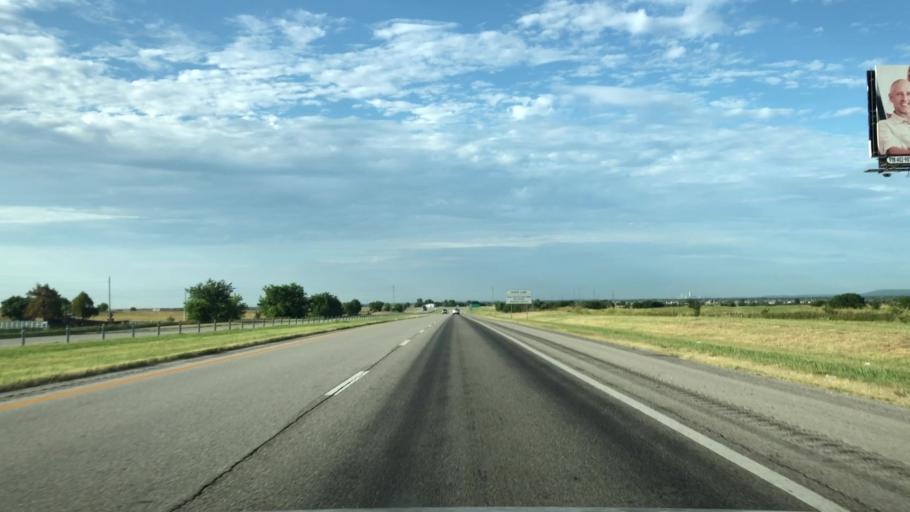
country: US
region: Oklahoma
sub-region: Osage County
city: Skiatook
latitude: 36.3600
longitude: -95.9208
